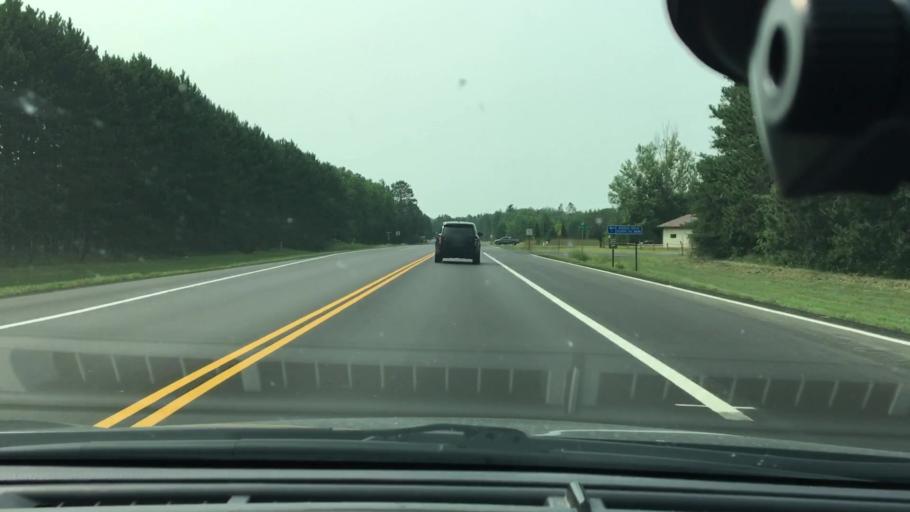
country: US
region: Minnesota
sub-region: Crow Wing County
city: Brainerd
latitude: 46.4294
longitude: -94.1755
